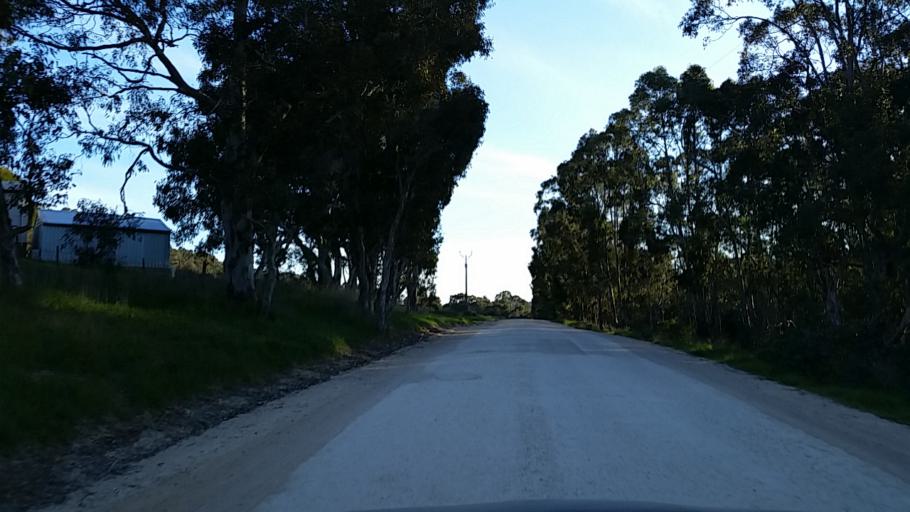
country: AU
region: South Australia
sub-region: Alexandrina
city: Mount Compass
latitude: -35.2933
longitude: 138.6878
